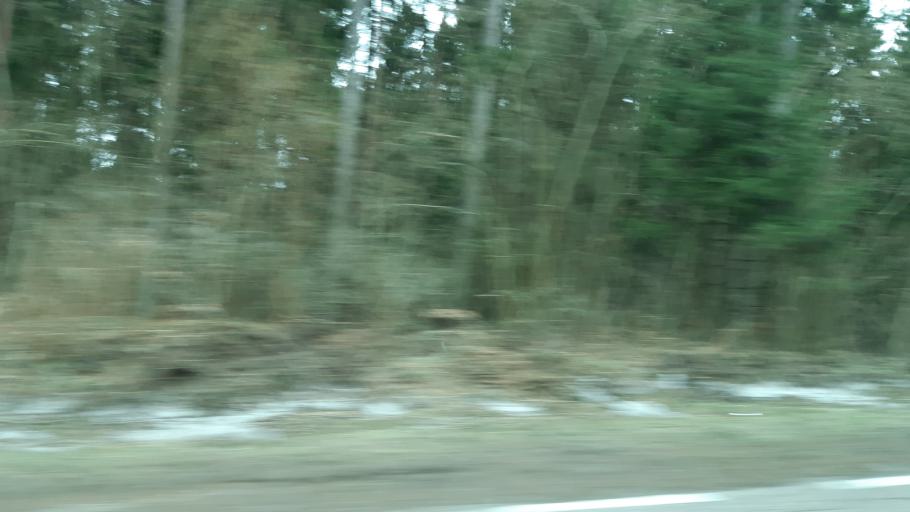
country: PL
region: Podlasie
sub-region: Suwalki
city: Suwalki
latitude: 54.3038
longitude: 22.9591
